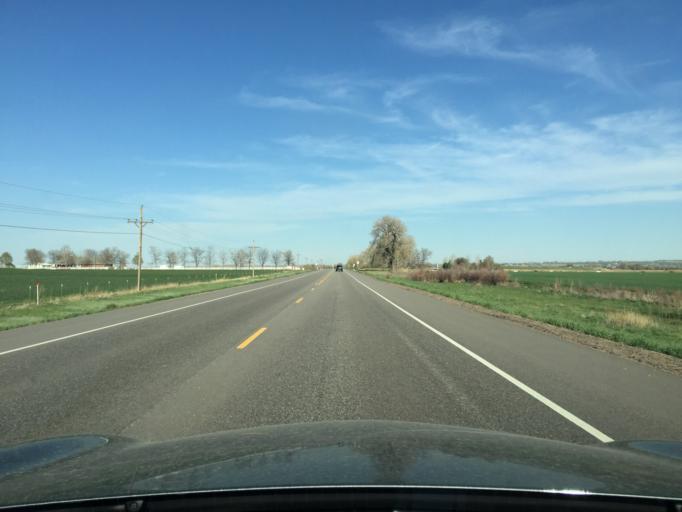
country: US
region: Colorado
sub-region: Boulder County
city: Niwot
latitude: 40.0874
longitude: -105.1110
